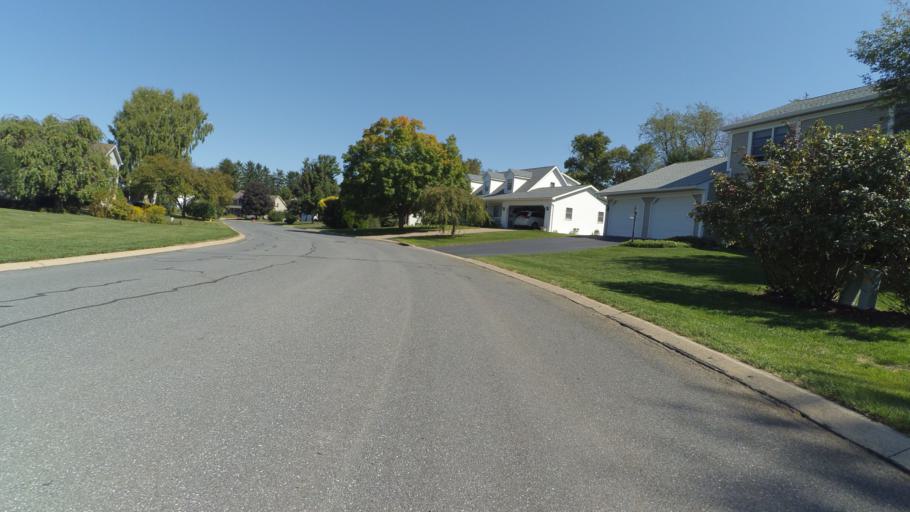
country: US
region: Pennsylvania
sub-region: Centre County
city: Pine Grove Mills
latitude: 40.7690
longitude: -77.8905
